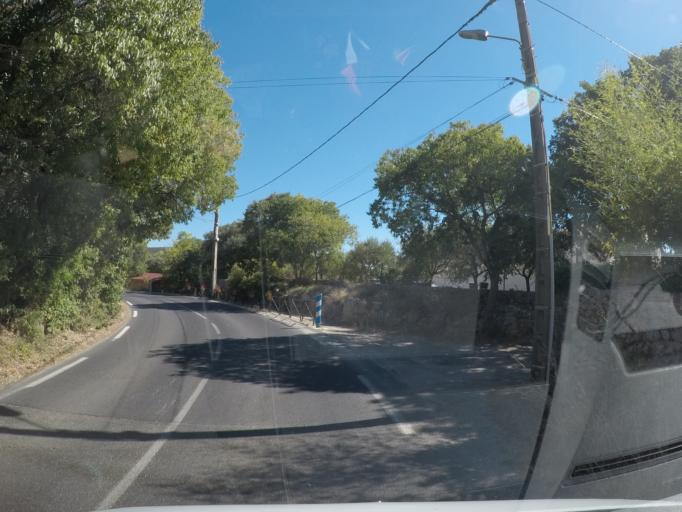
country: FR
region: Languedoc-Roussillon
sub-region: Departement de l'Herault
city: Aniane
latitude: 43.7120
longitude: 3.6153
